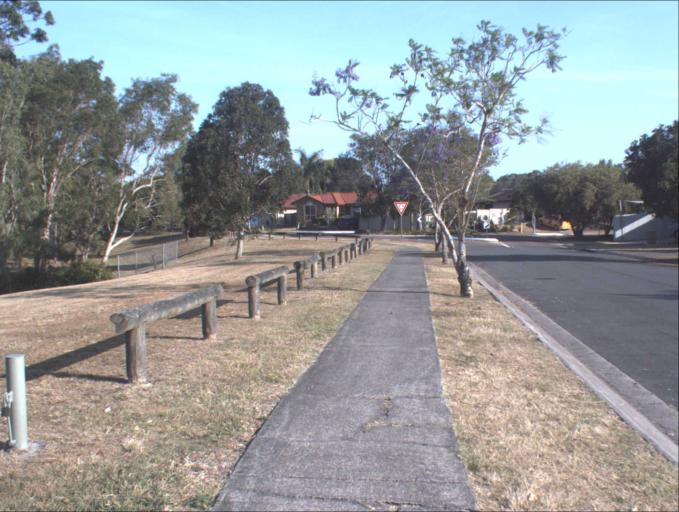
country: AU
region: Queensland
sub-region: Logan
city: Beenleigh
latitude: -27.6965
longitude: 153.1842
